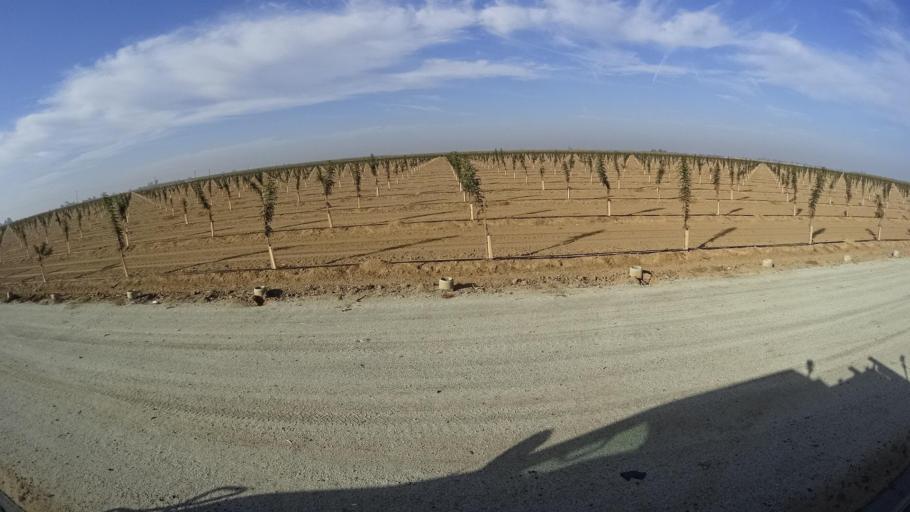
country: US
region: California
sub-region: Kern County
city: McFarland
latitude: 35.6553
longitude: -119.2046
